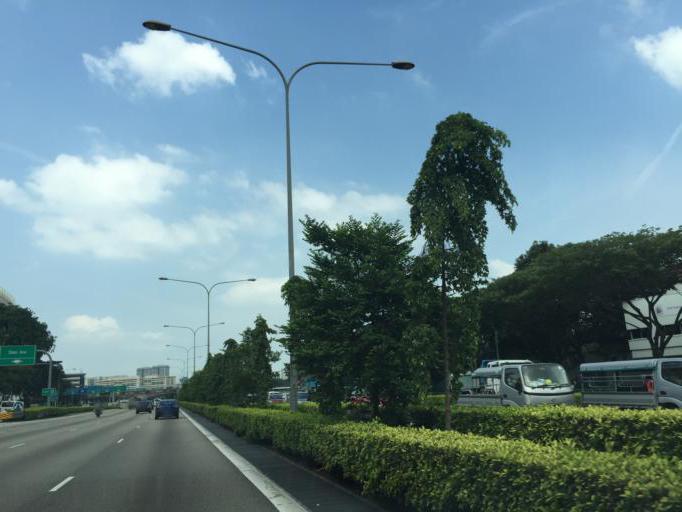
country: SG
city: Singapore
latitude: 1.3256
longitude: 103.8713
